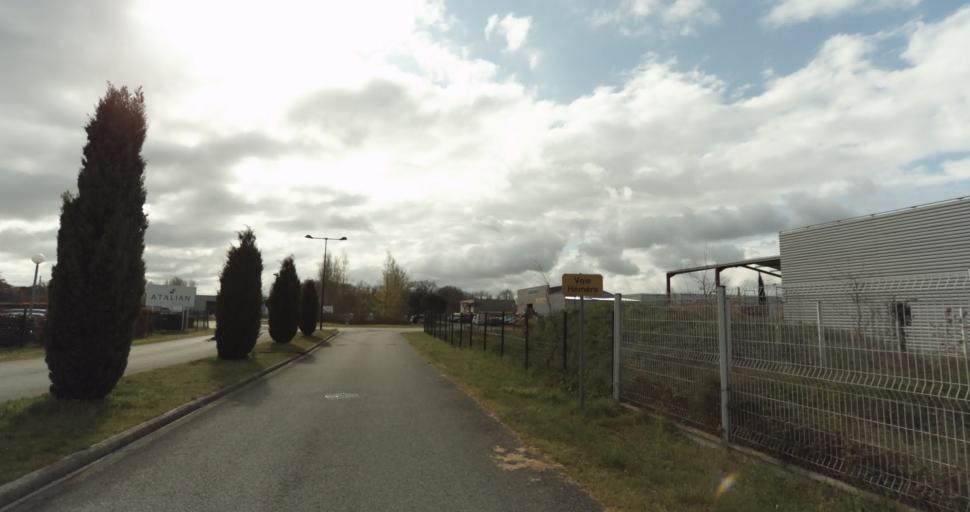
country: FR
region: Midi-Pyrenees
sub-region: Departement de la Haute-Garonne
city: Auterive
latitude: 43.3648
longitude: 1.4520
